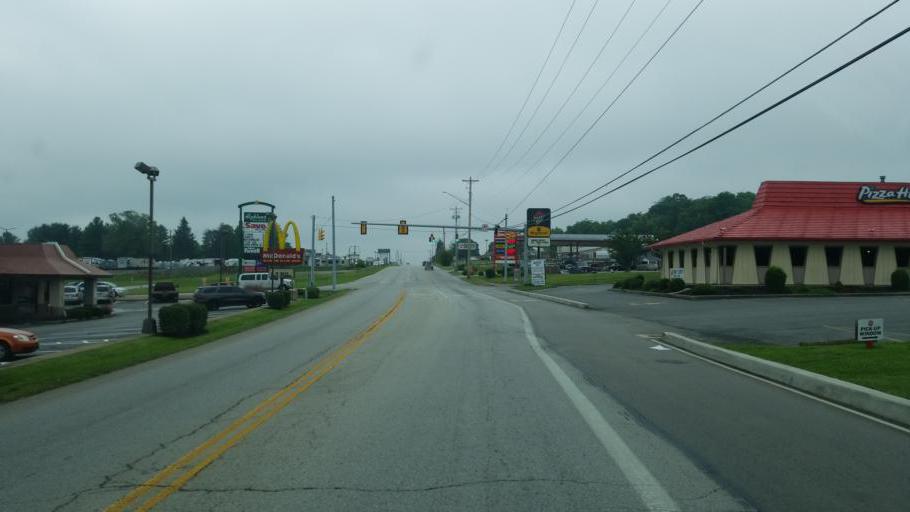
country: US
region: Ohio
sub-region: Highland County
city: Hillsboro
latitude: 39.2298
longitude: -83.6109
